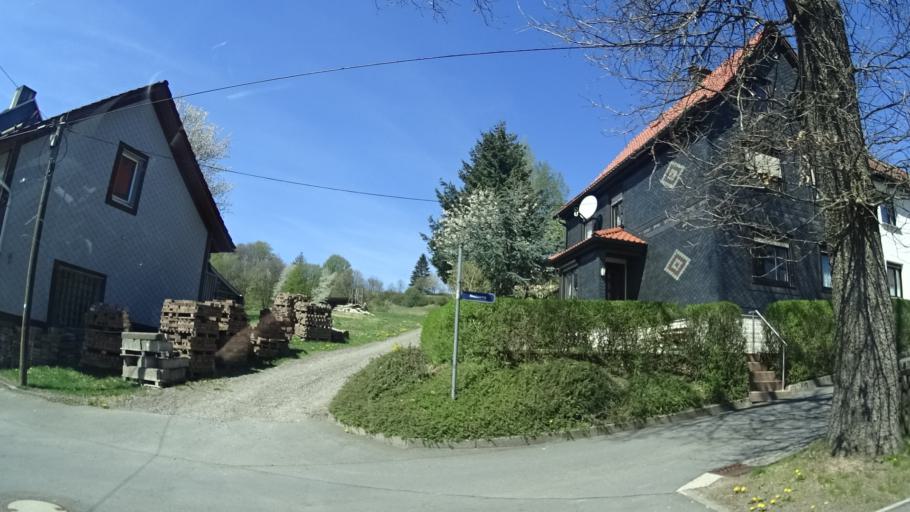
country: DE
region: Thuringia
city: Frauenwald
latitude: 50.5257
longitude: 10.8471
